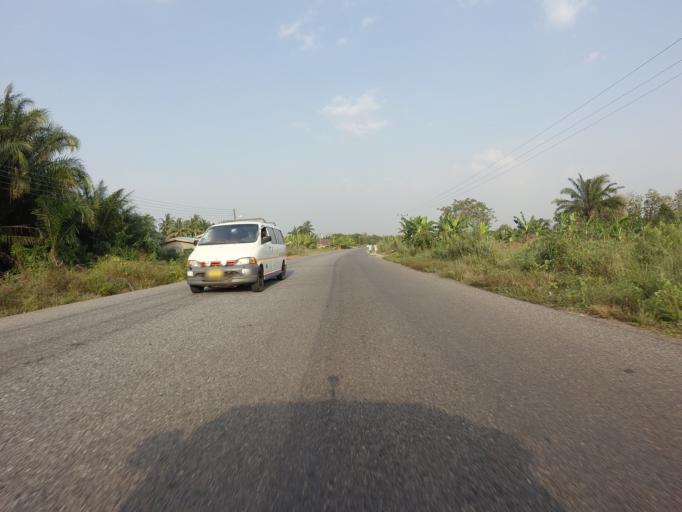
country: GH
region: Volta
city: Ho
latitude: 6.4184
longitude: 0.1775
